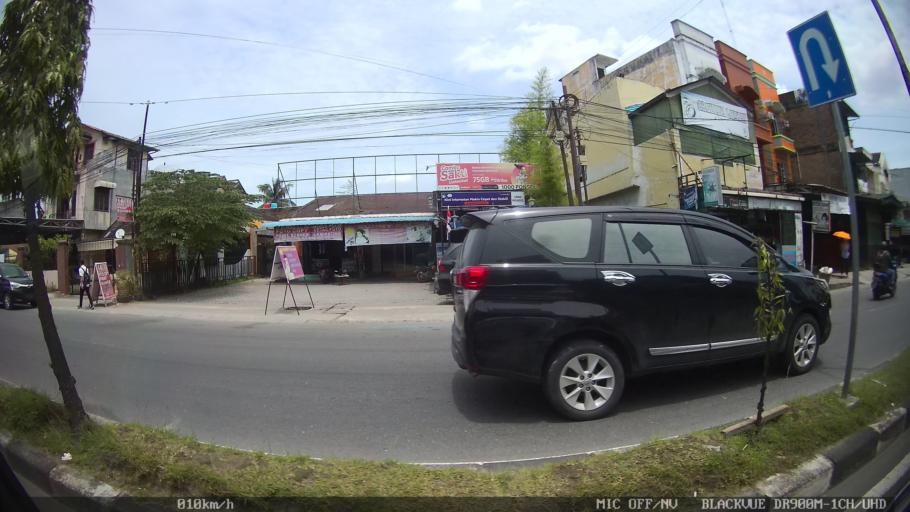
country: ID
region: North Sumatra
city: Sunggal
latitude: 3.5445
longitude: 98.6249
